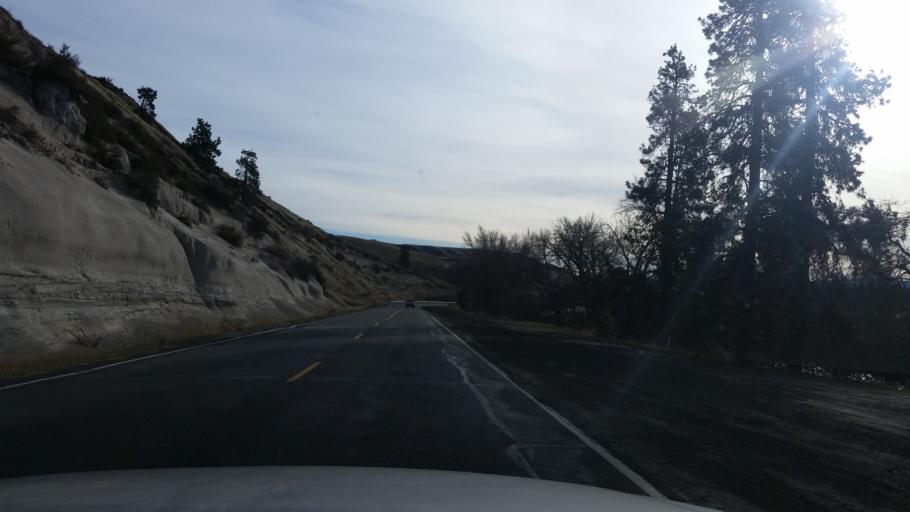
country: US
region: Washington
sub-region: Kittitas County
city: Ellensburg
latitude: 47.1007
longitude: -120.6950
